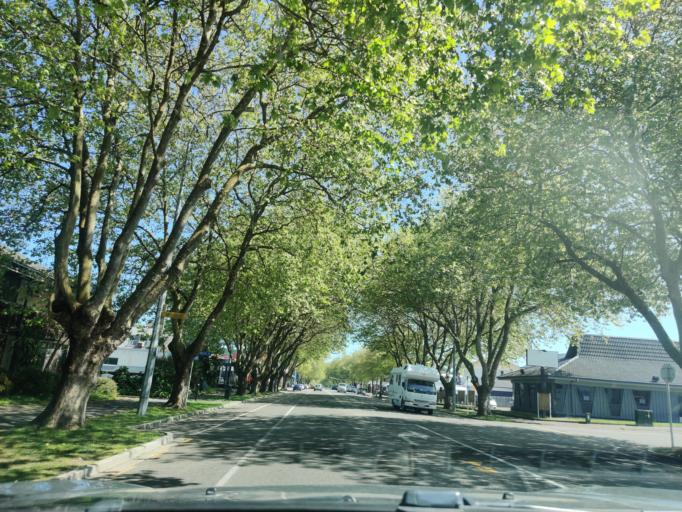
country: NZ
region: Manawatu-Wanganui
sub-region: Wanganui District
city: Wanganui
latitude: -39.9293
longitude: 175.0459
